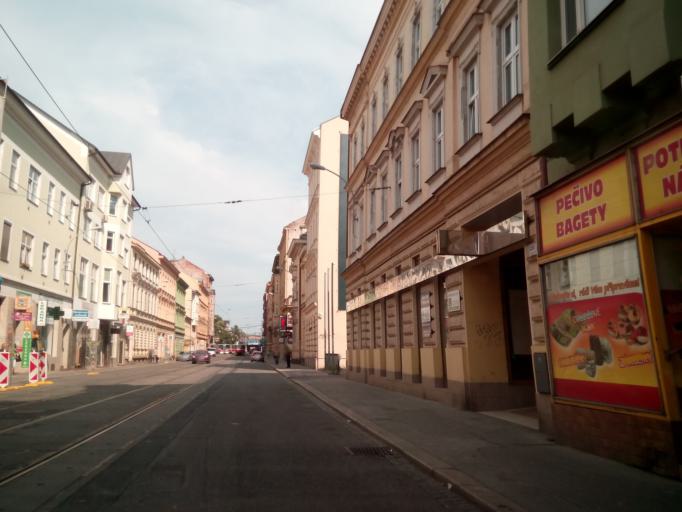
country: CZ
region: South Moravian
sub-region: Mesto Brno
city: Brno
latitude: 49.1892
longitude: 16.6038
